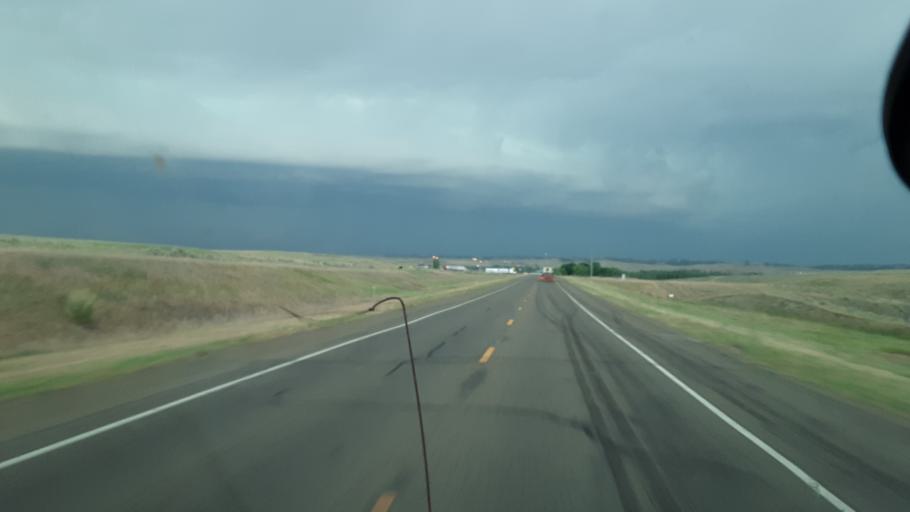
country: US
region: Montana
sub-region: Powder River County
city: Broadus
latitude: 45.4172
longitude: -105.3903
